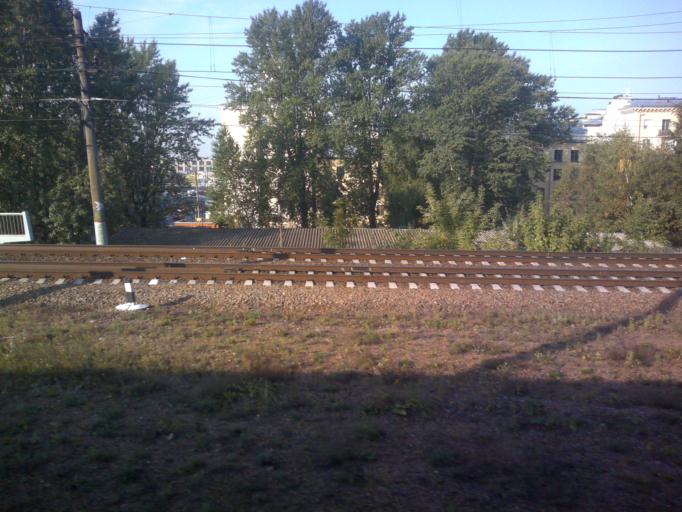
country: RU
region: Leningrad
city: Sampsonievskiy
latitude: 59.9851
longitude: 30.3388
